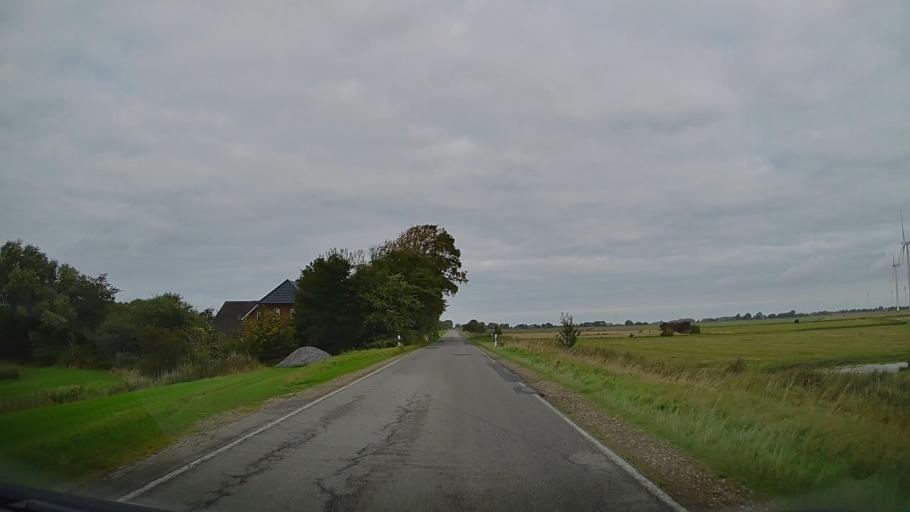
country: DE
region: Schleswig-Holstein
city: Emmelsbull-Horsbull
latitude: 54.7904
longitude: 8.7274
